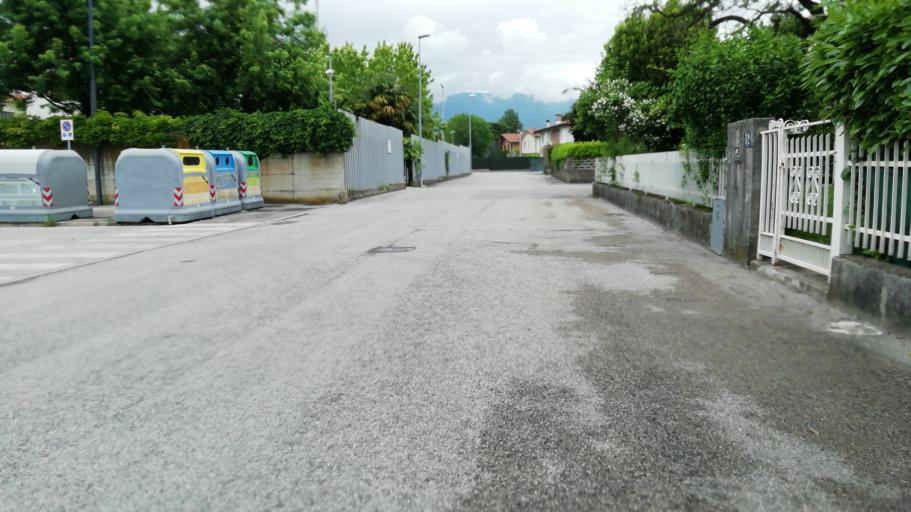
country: IT
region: Veneto
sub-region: Provincia di Vicenza
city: Thiene
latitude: 45.7135
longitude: 11.4784
